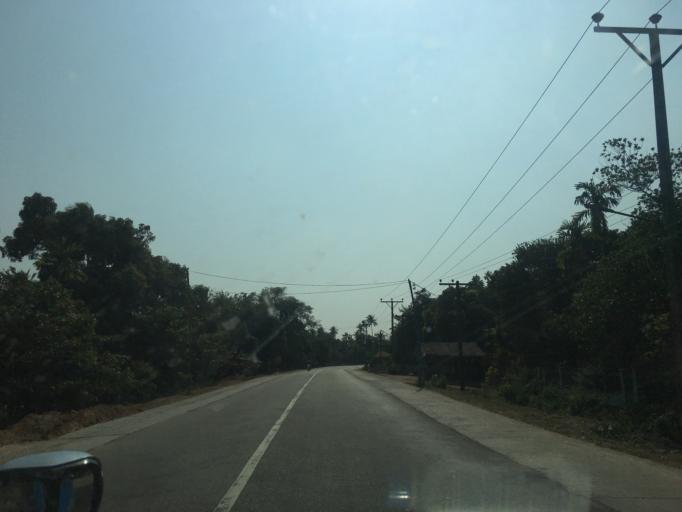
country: MM
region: Mon
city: Martaban
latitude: 16.6013
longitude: 97.5020
